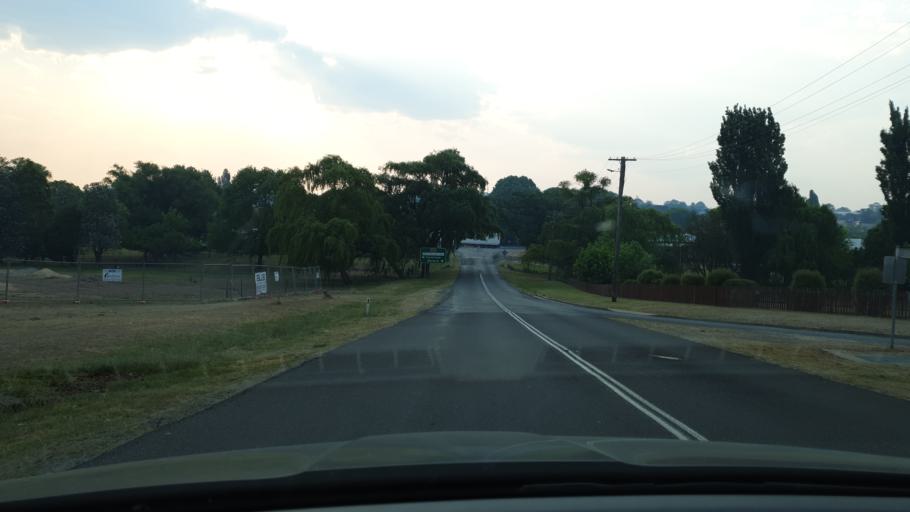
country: AU
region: New South Wales
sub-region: Tenterfield Municipality
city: Carrolls Creek
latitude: -29.0459
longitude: 152.0227
